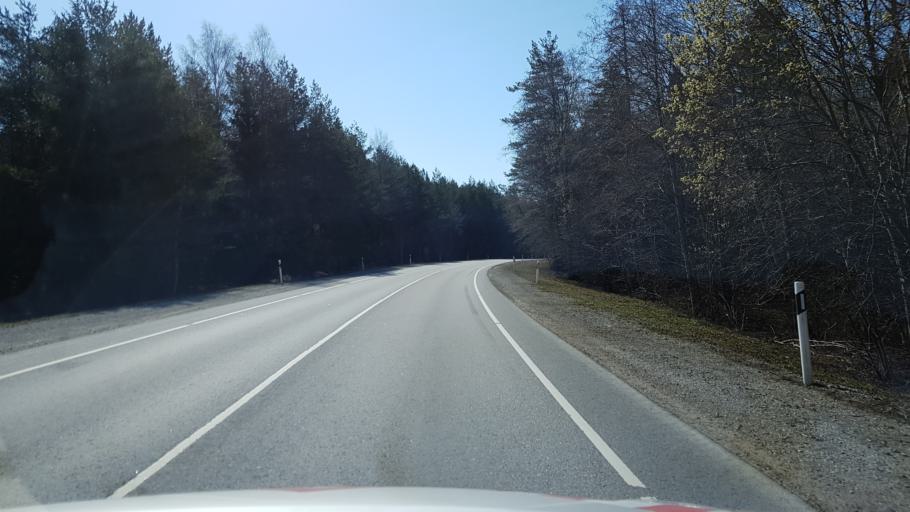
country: EE
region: Ida-Virumaa
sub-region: Kohtla-Jaerve linn
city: Kohtla-Jarve
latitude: 59.3344
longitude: 27.2642
